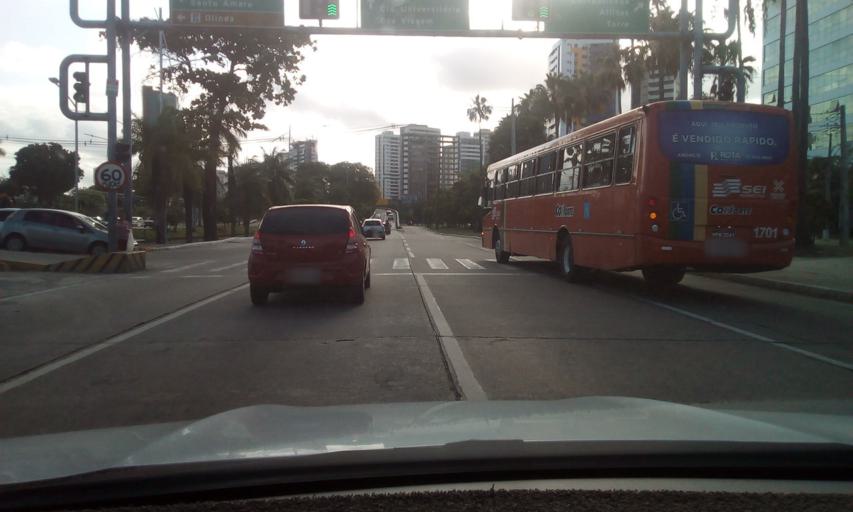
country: BR
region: Pernambuco
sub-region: Recife
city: Recife
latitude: -8.0435
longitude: -34.8873
